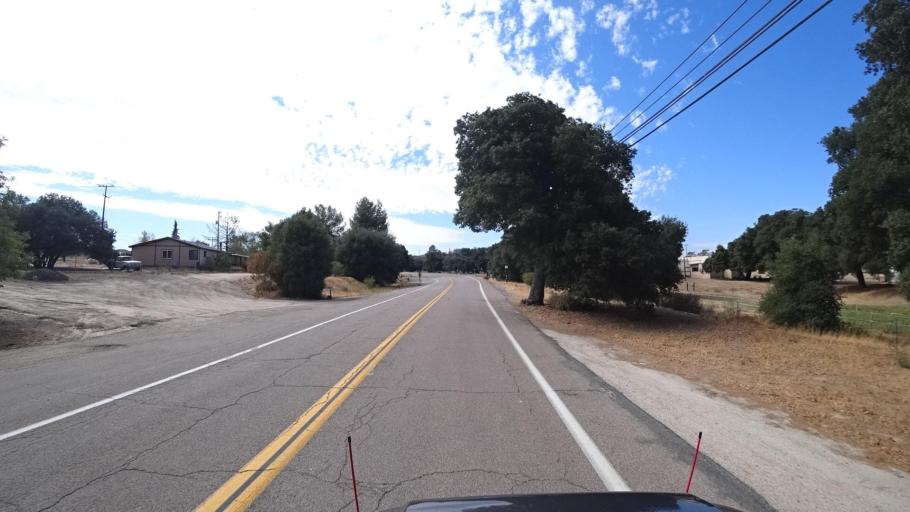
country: MX
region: Baja California
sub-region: Tecate
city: Cereso del Hongo
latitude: 32.6689
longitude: -116.2883
